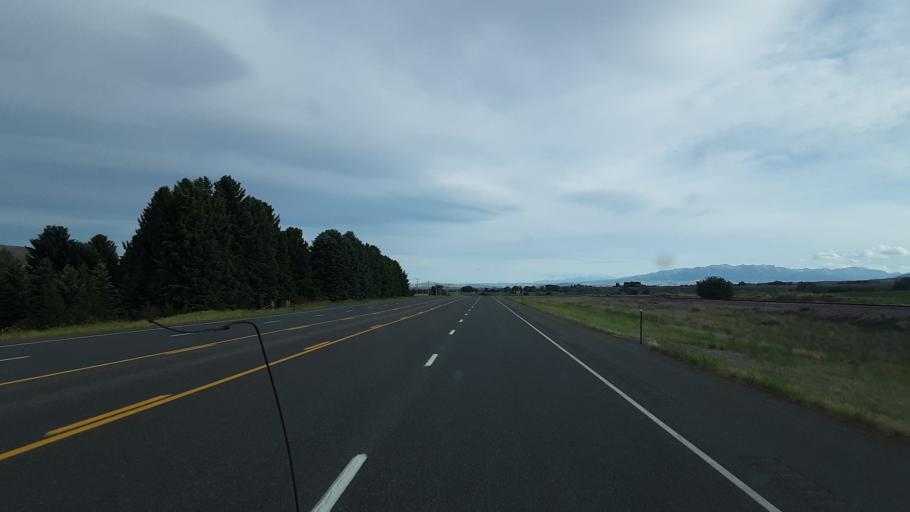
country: US
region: Wyoming
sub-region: Park County
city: Cody
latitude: 44.6473
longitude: -108.9523
